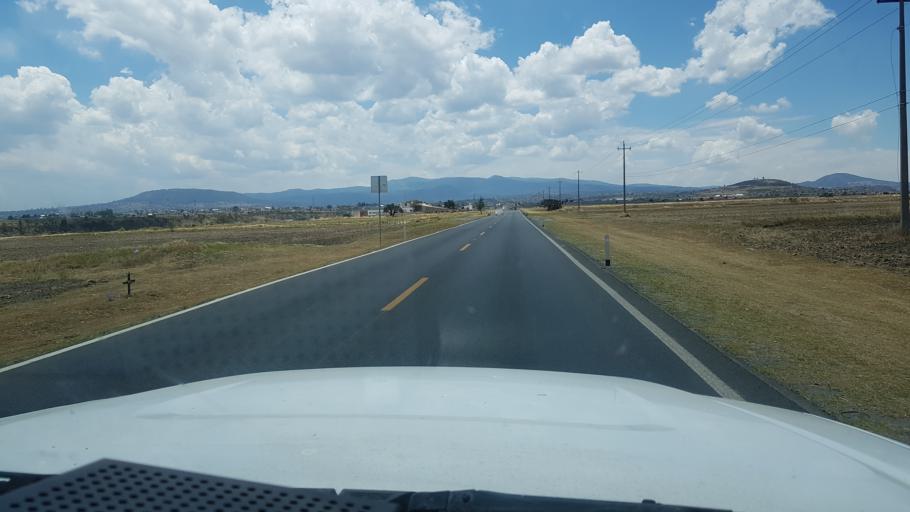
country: MX
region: Hidalgo
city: Calpulalpan
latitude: 19.6112
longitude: -98.5580
